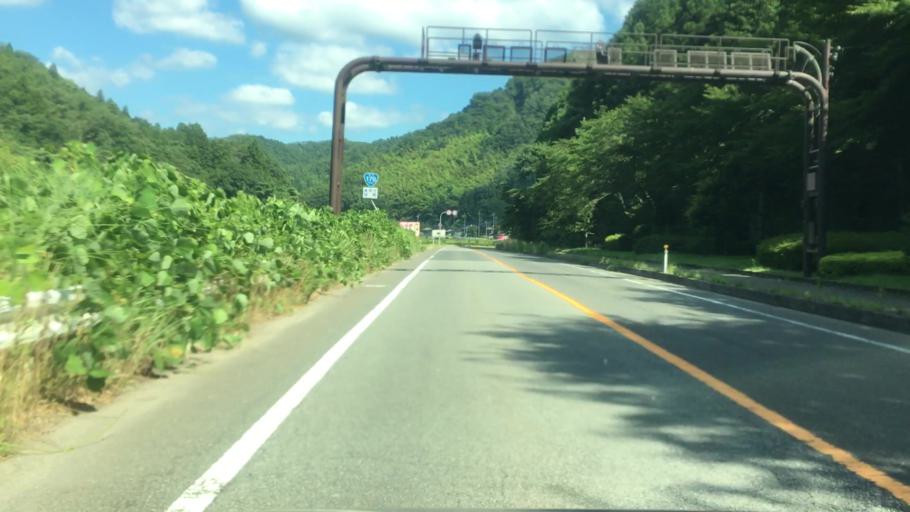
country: JP
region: Hyogo
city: Toyooka
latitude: 35.5678
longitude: 134.7826
